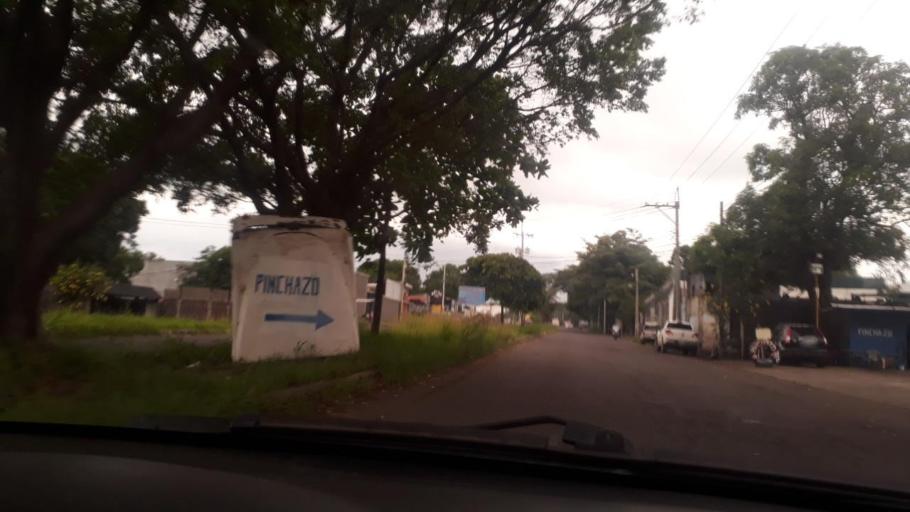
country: GT
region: Escuintla
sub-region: Municipio de Escuintla
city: Escuintla
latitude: 14.2783
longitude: -90.7642
